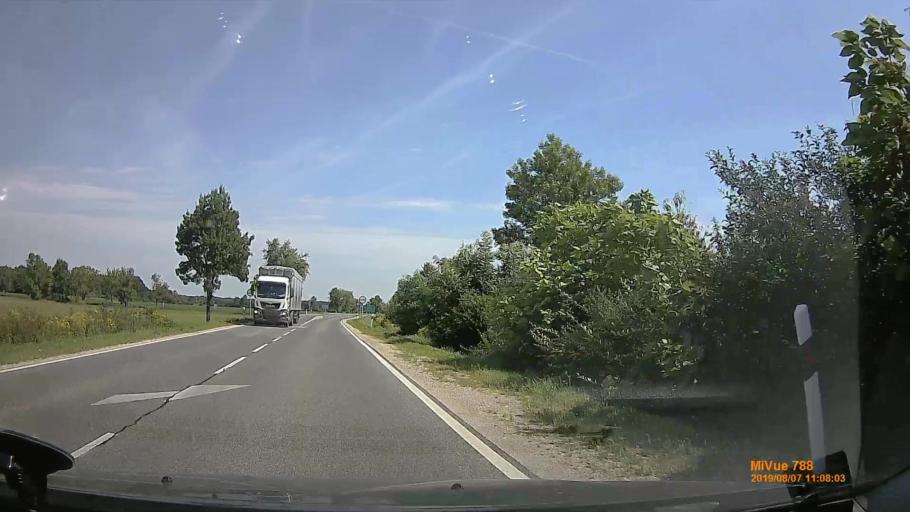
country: HU
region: Zala
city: Lenti
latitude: 46.6308
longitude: 16.4742
